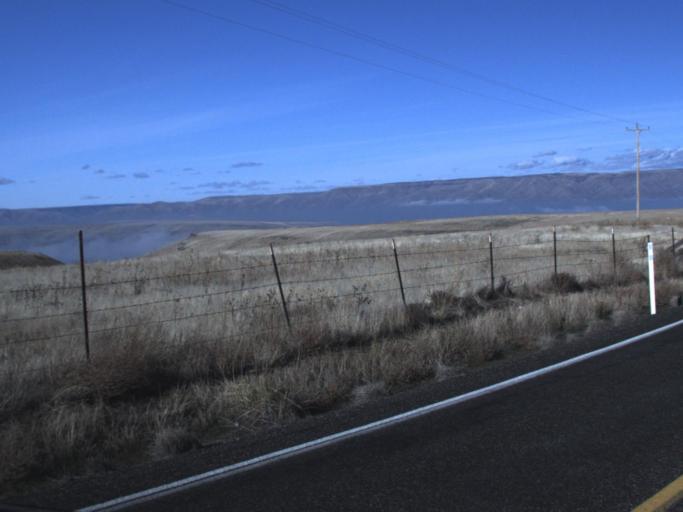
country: US
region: Washington
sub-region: Asotin County
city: Asotin
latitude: 46.2994
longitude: -117.0435
